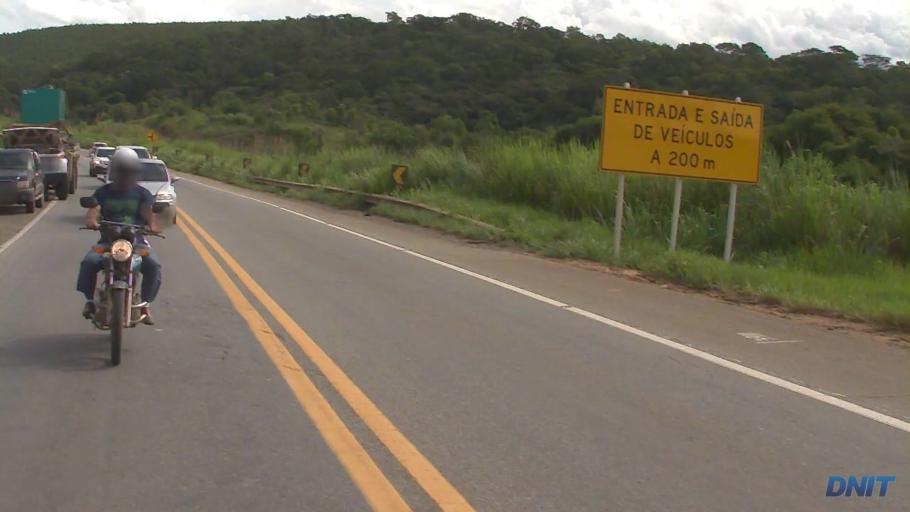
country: BR
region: Minas Gerais
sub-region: Ipaba
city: Ipaba
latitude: -19.3539
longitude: -42.4350
